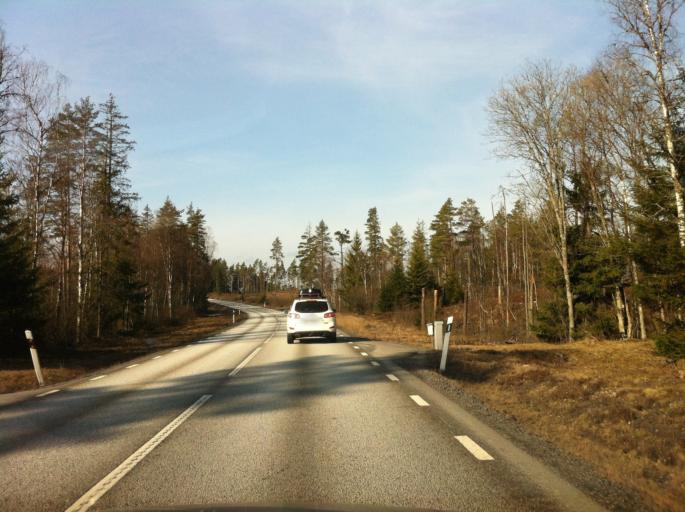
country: SE
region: Joenkoeping
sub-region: Habo Kommun
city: Habo
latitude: 57.8639
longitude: 13.9875
